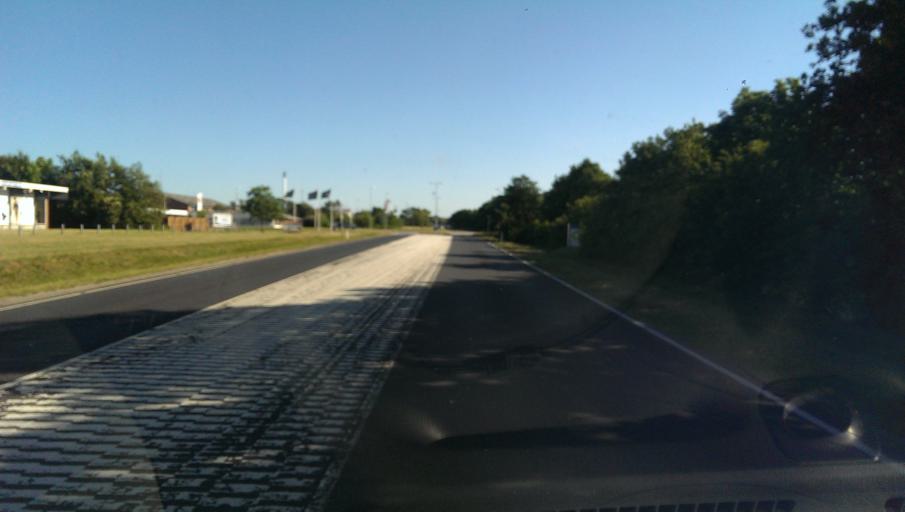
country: DK
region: South Denmark
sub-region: Esbjerg Kommune
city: Esbjerg
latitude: 55.5115
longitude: 8.4059
